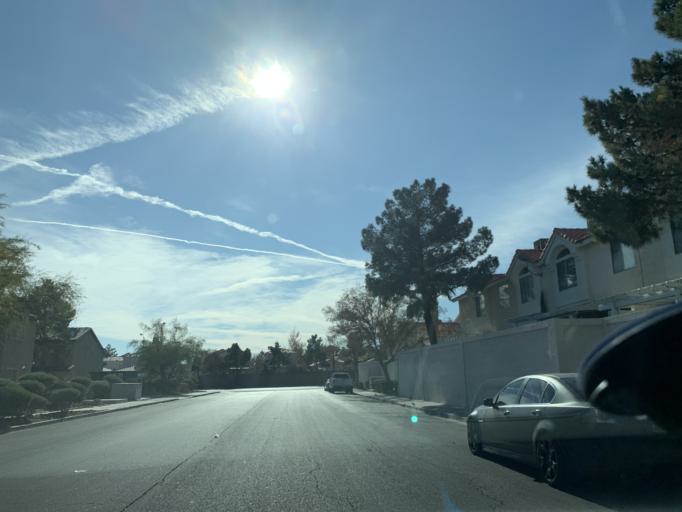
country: US
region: Nevada
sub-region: Clark County
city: Spring Valley
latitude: 36.0937
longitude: -115.2209
